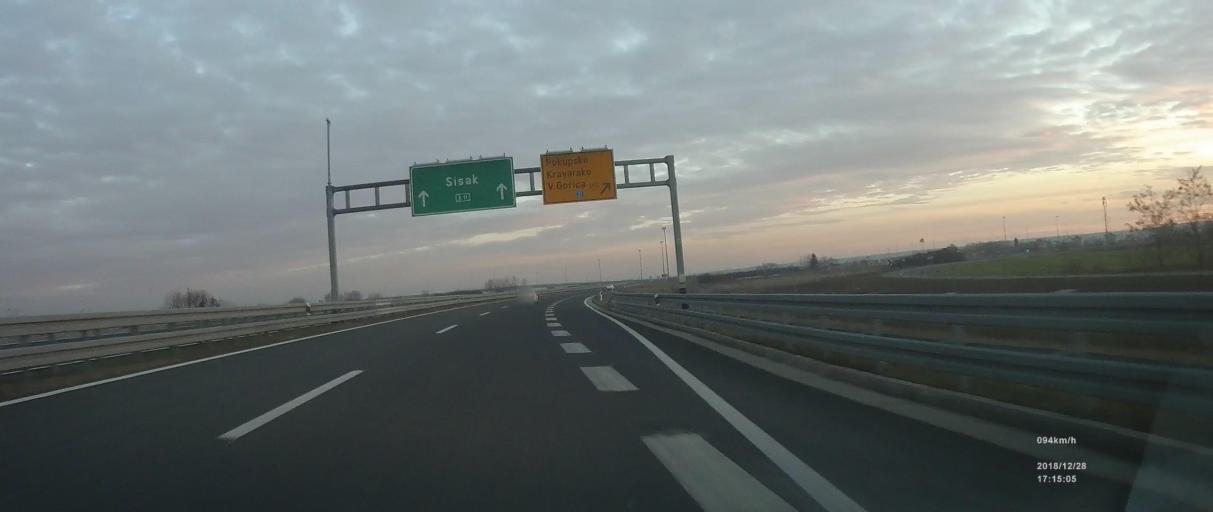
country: HR
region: Zagrebacka
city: Gradici
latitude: 45.6975
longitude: 16.0607
